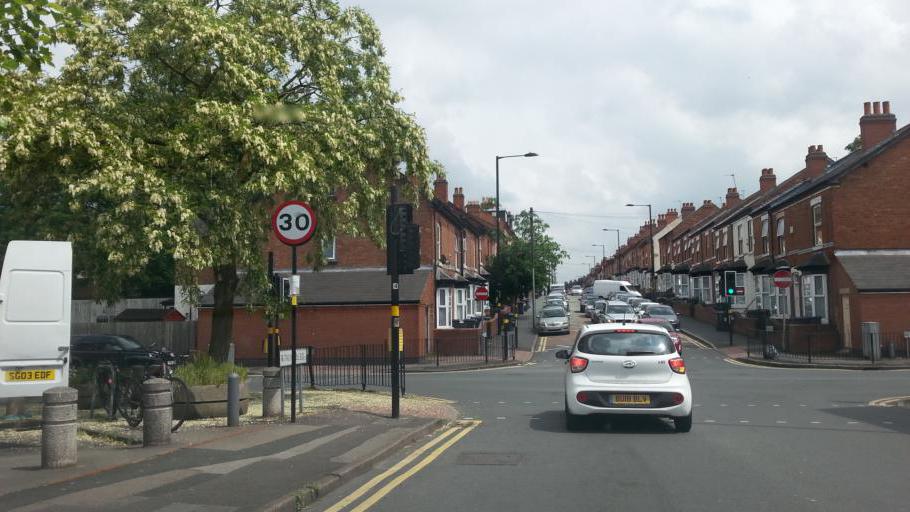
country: GB
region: England
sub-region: City and Borough of Birmingham
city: Birmingham
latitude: 52.4533
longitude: -1.8738
